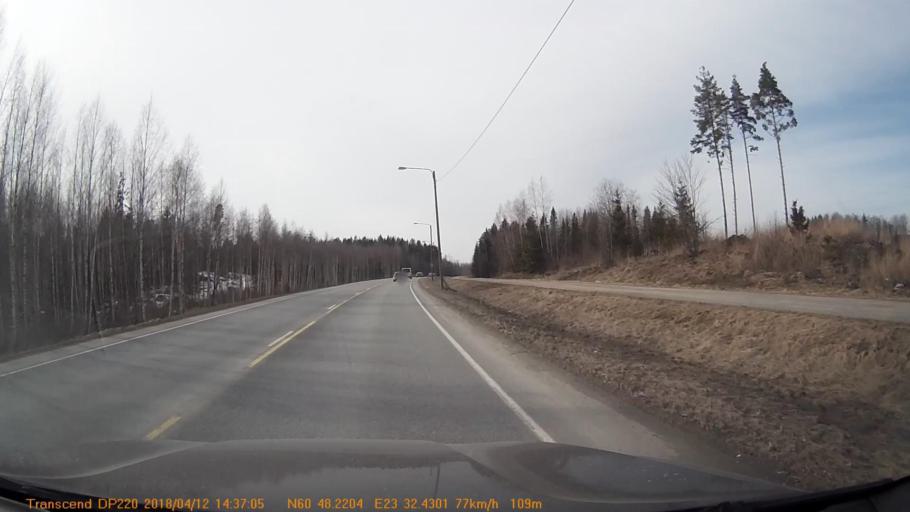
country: FI
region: Haeme
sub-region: Forssa
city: Jokioinen
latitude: 60.8041
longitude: 23.5376
